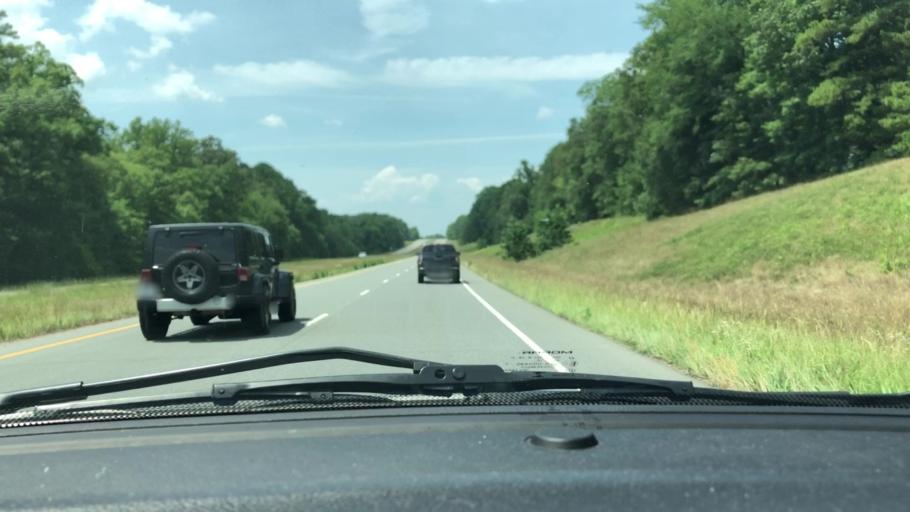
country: US
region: North Carolina
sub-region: Chatham County
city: Farmville
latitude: 35.5298
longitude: -79.2327
